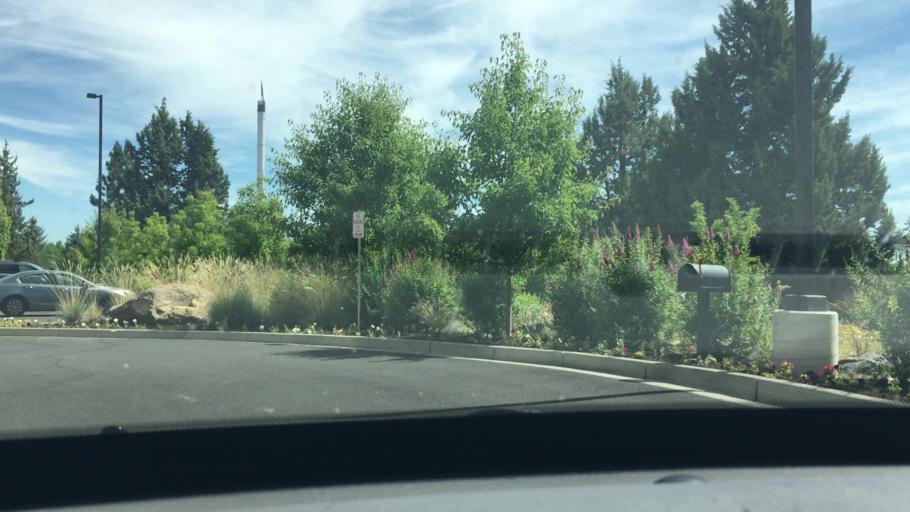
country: US
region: Oregon
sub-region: Deschutes County
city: Bend
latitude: 44.0442
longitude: -121.3180
